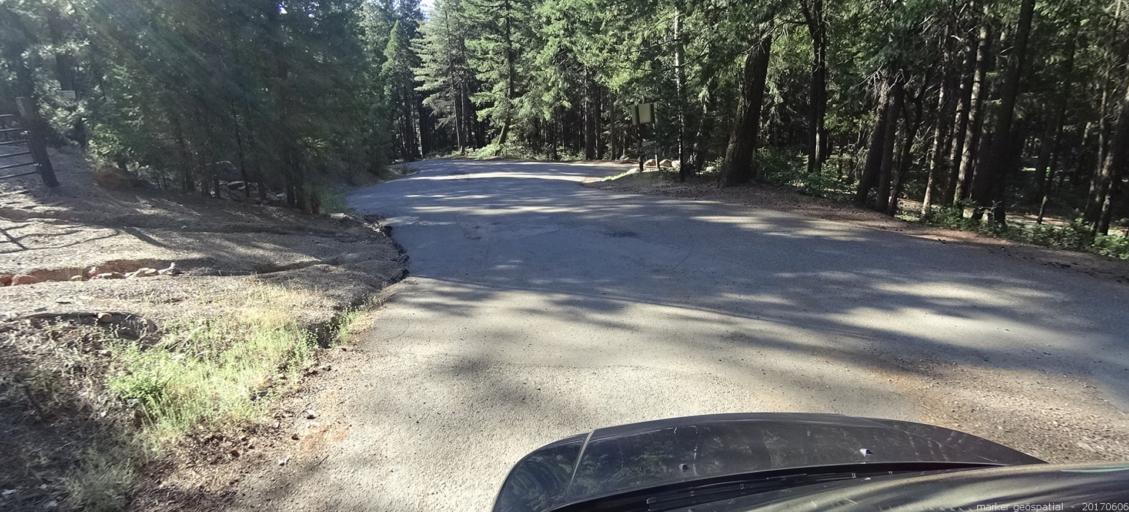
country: US
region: California
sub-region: Siskiyou County
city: Dunsmuir
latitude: 41.1870
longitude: -122.2973
